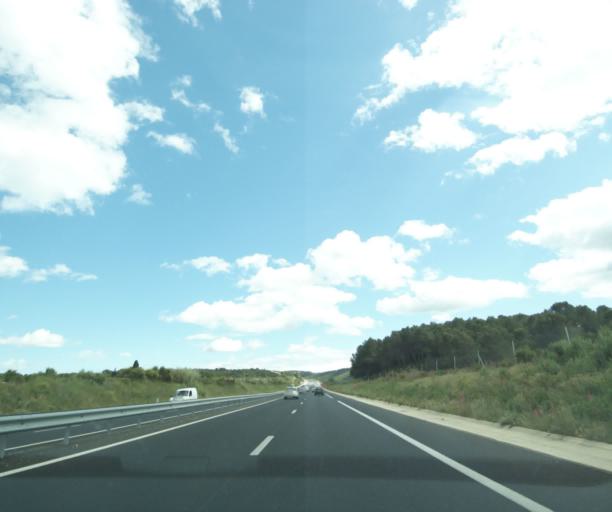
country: FR
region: Languedoc-Roussillon
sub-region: Departement de l'Herault
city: Gignac
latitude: 43.6362
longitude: 3.5826
